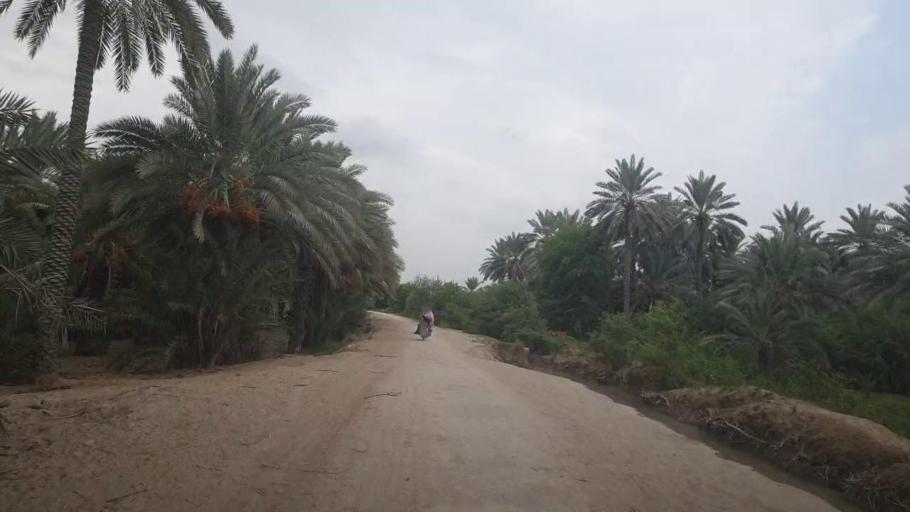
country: PK
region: Sindh
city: Khairpur
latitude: 27.5832
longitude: 68.7123
